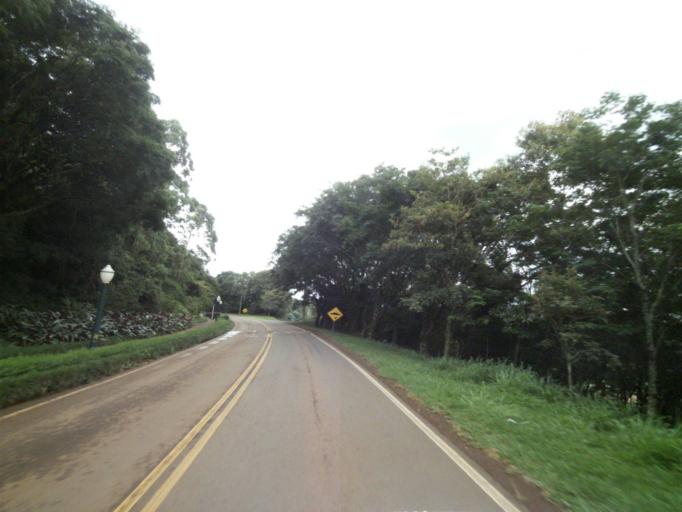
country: BR
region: Parana
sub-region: Guaraniacu
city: Guaraniacu
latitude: -25.0999
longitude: -52.8881
